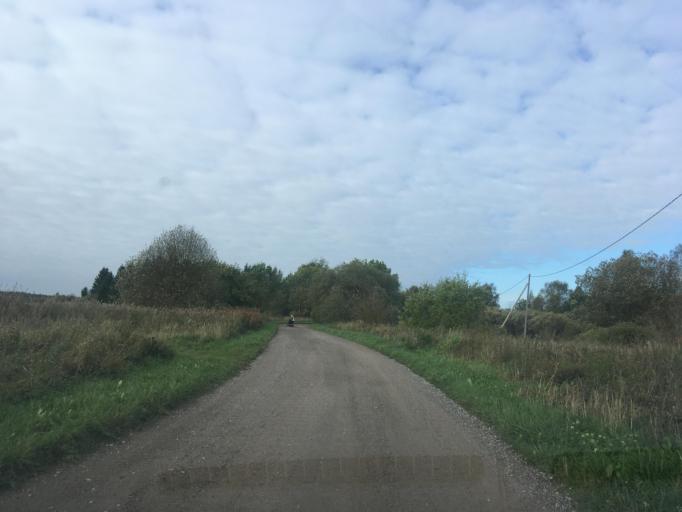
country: EE
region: Harju
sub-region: Maardu linn
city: Maardu
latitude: 59.4527
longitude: 25.0588
